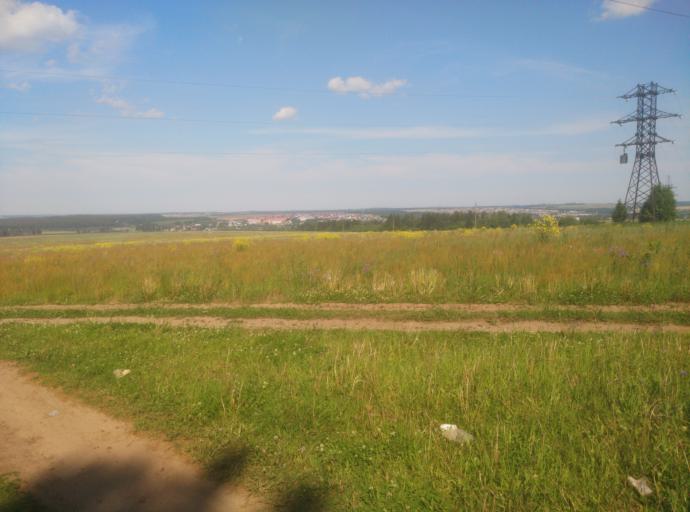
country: RU
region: Udmurtiya
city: Khokhryaki
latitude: 56.7912
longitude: 53.3311
